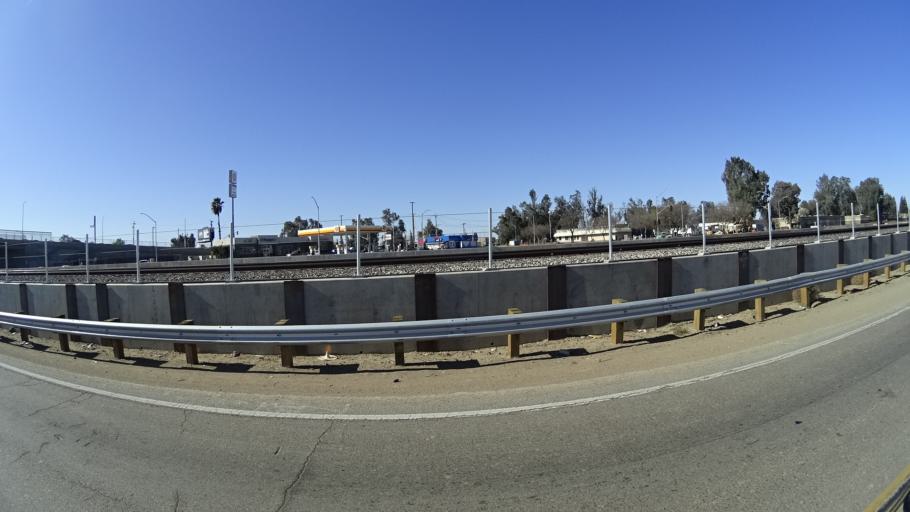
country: US
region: California
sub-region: Fresno County
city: West Park
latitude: 36.7950
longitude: -119.8617
